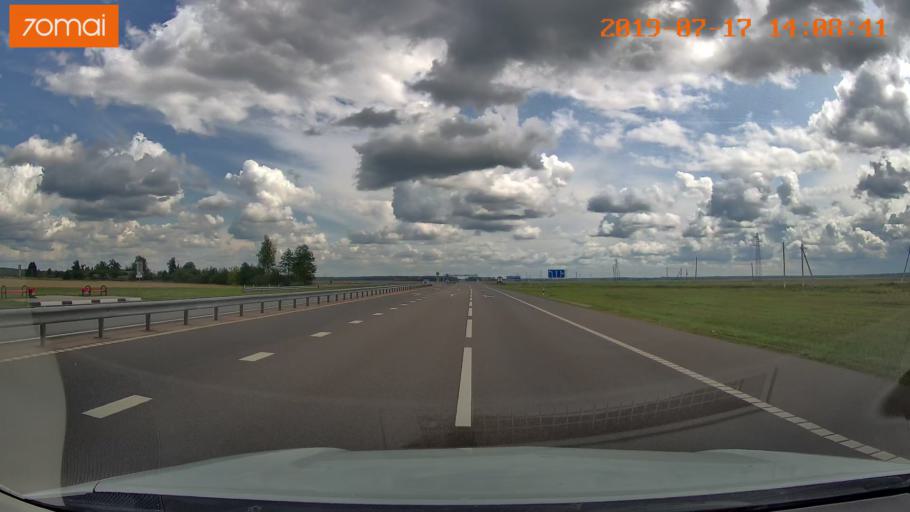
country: BY
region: Mogilev
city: Yalizava
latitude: 53.2350
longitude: 28.9743
